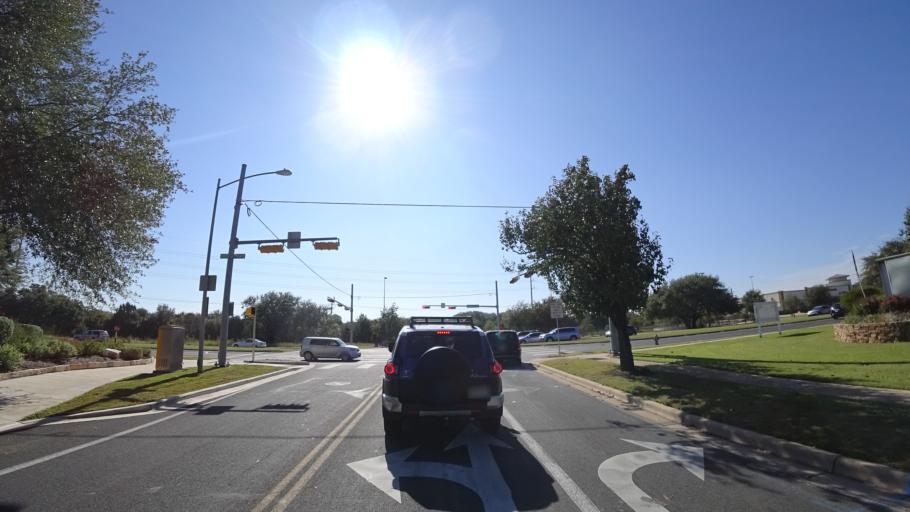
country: US
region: Texas
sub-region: Travis County
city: Shady Hollow
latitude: 30.1990
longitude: -97.8625
